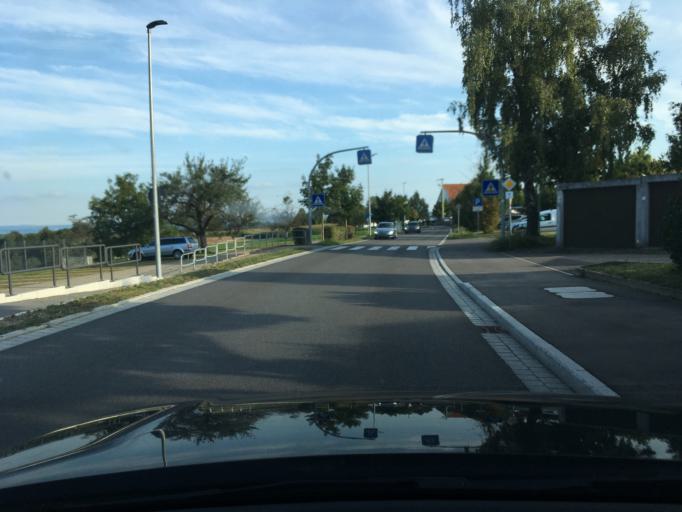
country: DE
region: Baden-Wuerttemberg
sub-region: Regierungsbezirk Stuttgart
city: Schorndorf
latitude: 48.7741
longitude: 9.5562
